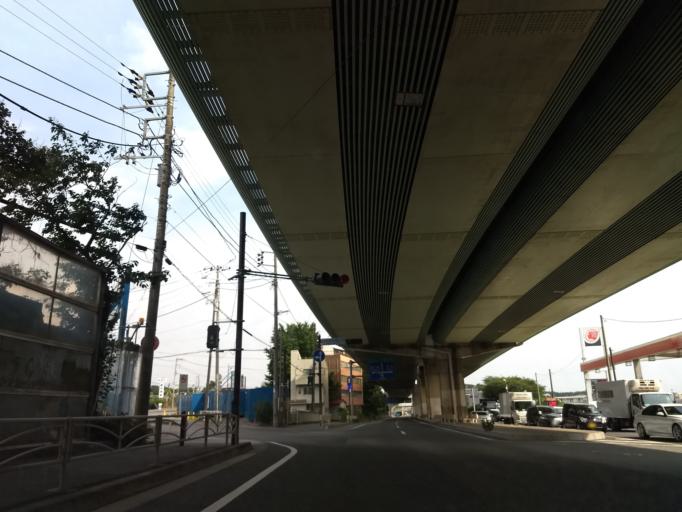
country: JP
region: Kanagawa
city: Minami-rinkan
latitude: 35.5017
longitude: 139.4908
